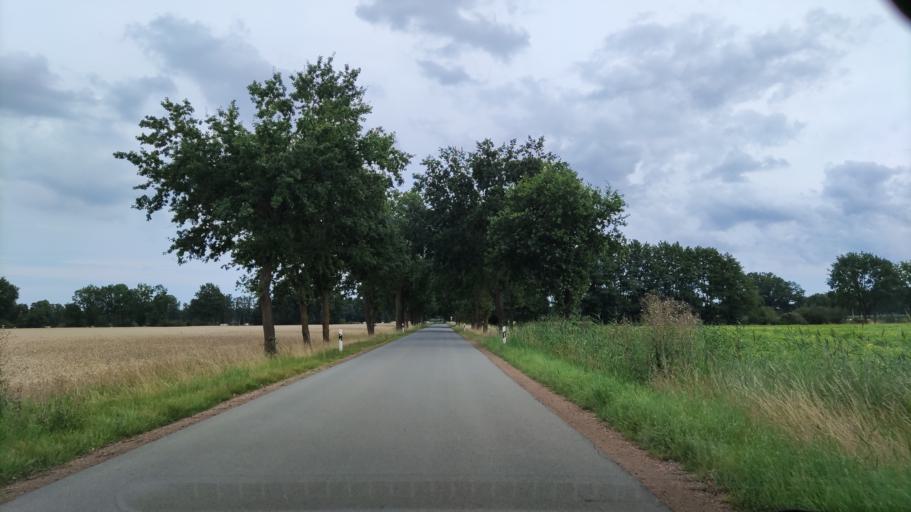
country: DE
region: Lower Saxony
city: Dannenberg
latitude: 53.0835
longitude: 11.1344
